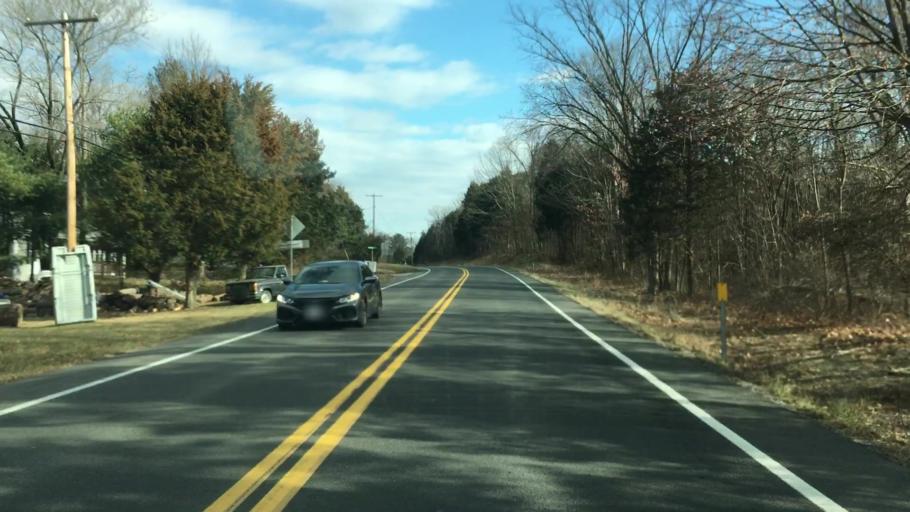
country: US
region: Virginia
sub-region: Warren County
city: Front Royal
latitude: 38.9554
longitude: -78.2525
